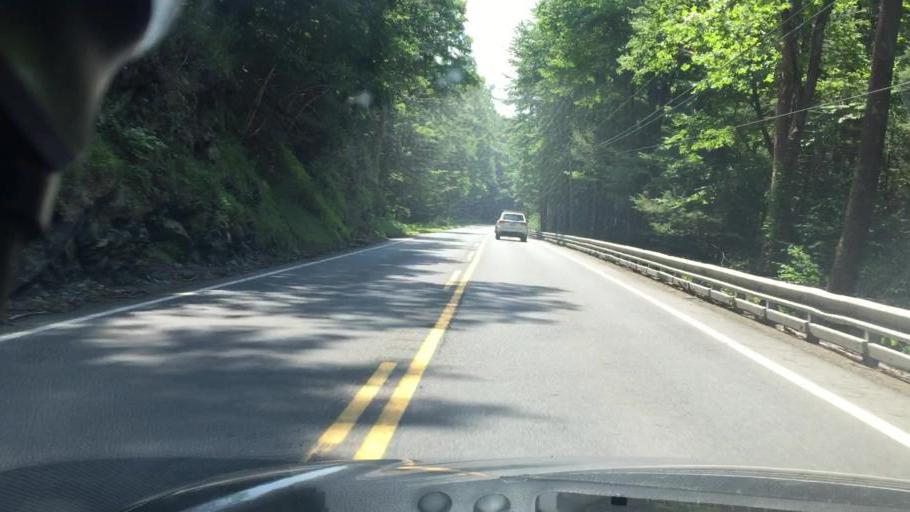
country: US
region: Pennsylvania
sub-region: Northumberland County
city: Elysburg
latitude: 40.8945
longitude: -76.5093
